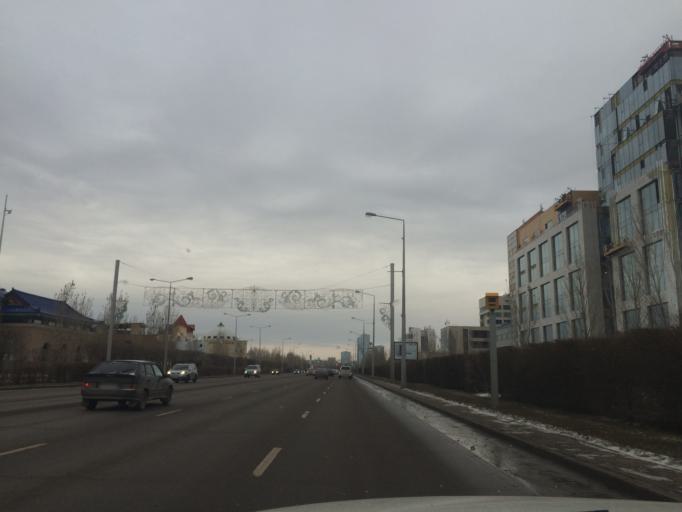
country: KZ
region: Astana Qalasy
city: Astana
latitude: 51.1392
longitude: 71.4099
